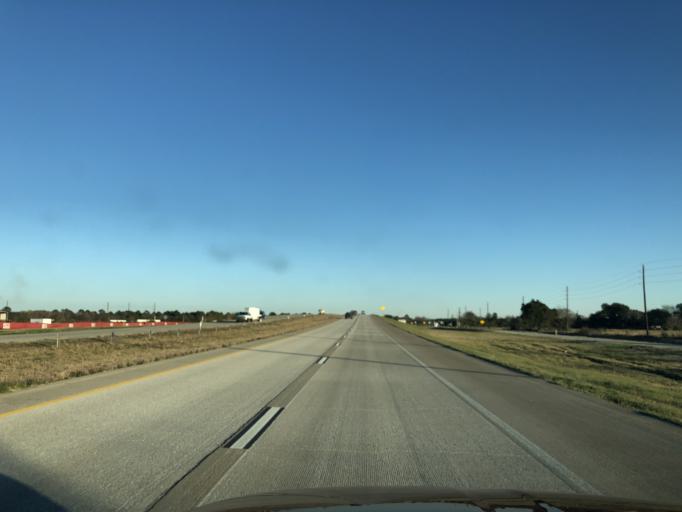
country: US
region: Texas
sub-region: Harris County
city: Cypress
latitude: 30.0532
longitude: -95.7019
